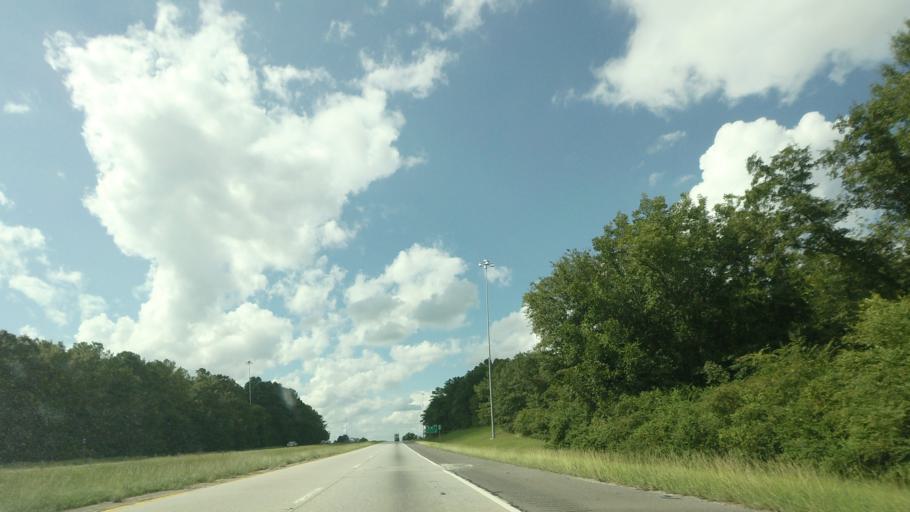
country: US
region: Georgia
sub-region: Bibb County
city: Macon
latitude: 32.7939
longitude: -83.5652
